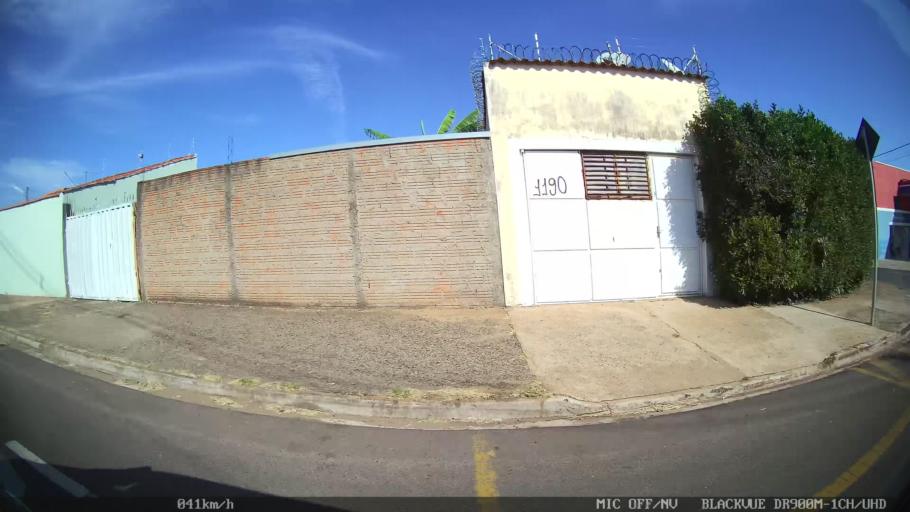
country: BR
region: Sao Paulo
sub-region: Franca
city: Franca
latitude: -20.5083
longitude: -47.4241
